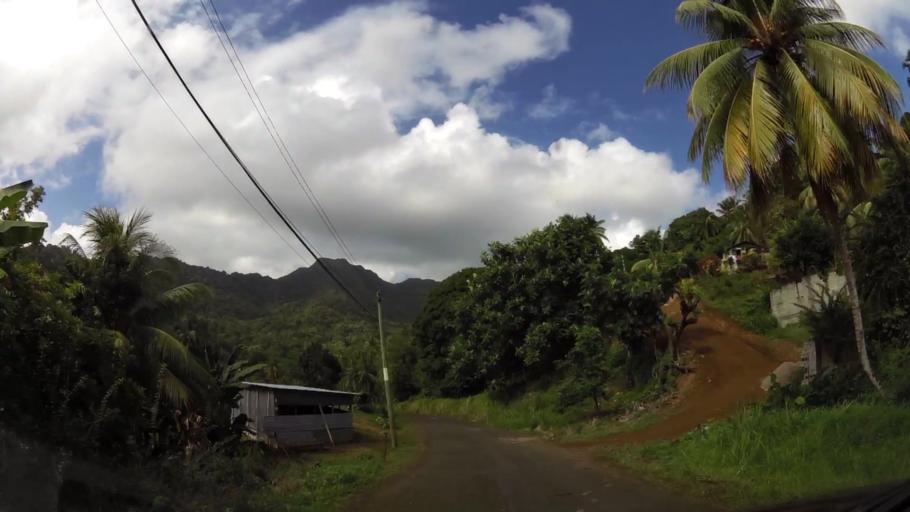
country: DM
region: Saint David
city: Castle Bruce
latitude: 15.4656
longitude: -61.2489
